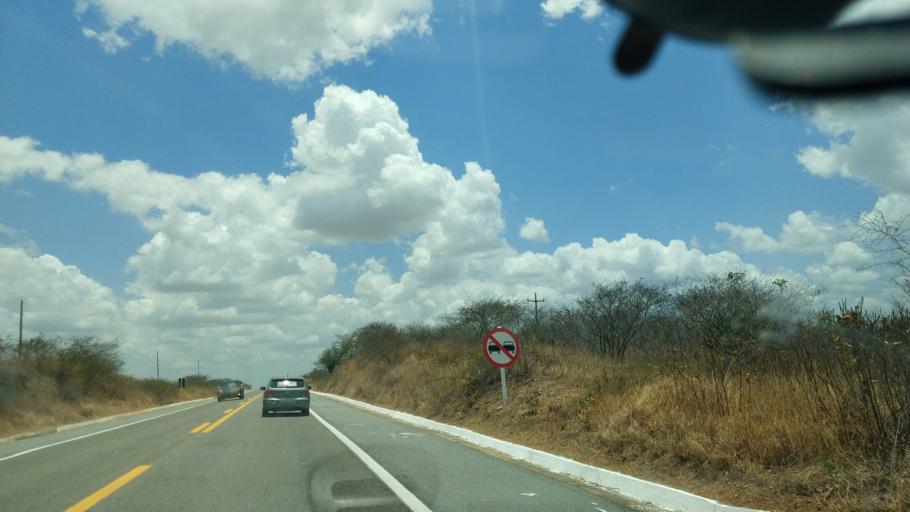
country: BR
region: Rio Grande do Norte
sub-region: Cerro Cora
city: Cerro Cora
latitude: -6.1960
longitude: -36.2649
